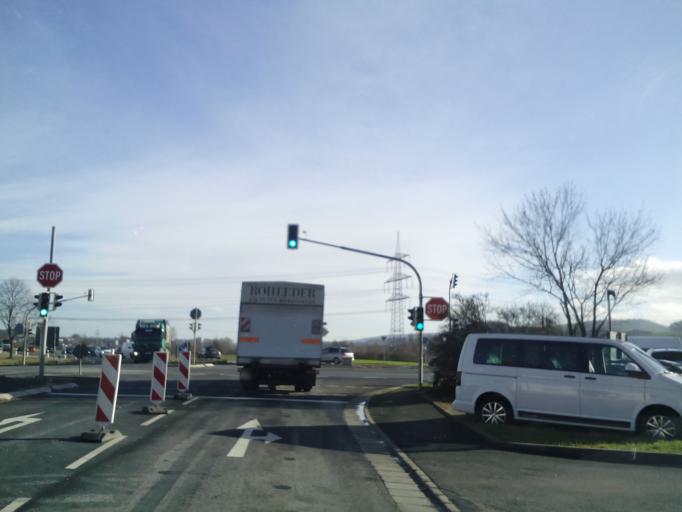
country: DE
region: Bavaria
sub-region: Upper Franconia
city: Hochstadt am Main
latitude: 50.1605
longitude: 11.1845
